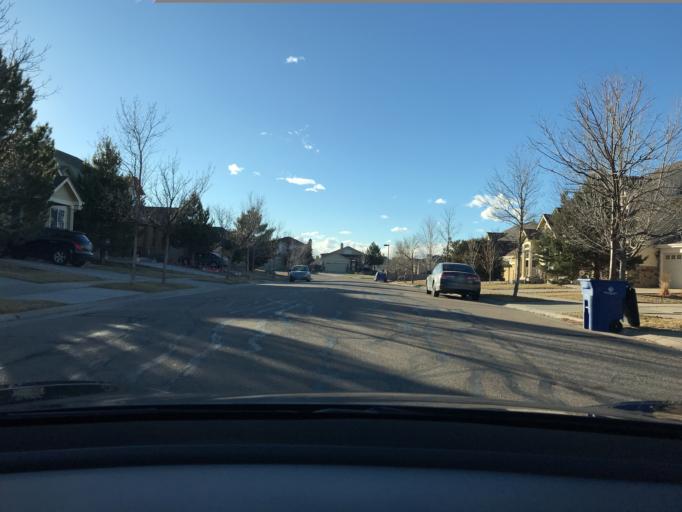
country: US
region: Colorado
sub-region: Boulder County
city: Erie
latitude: 40.0063
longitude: -105.0144
